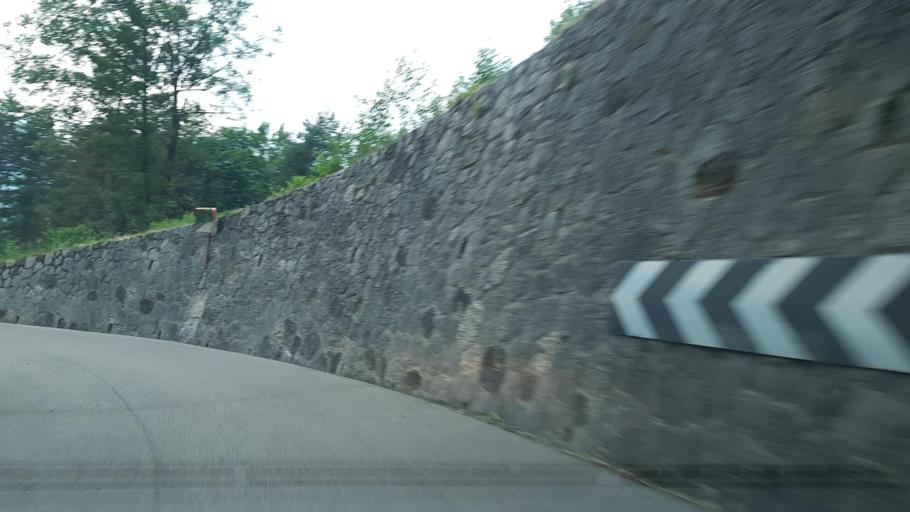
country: IT
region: Friuli Venezia Giulia
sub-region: Provincia di Udine
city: Pontebba
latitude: 46.5192
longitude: 13.2957
